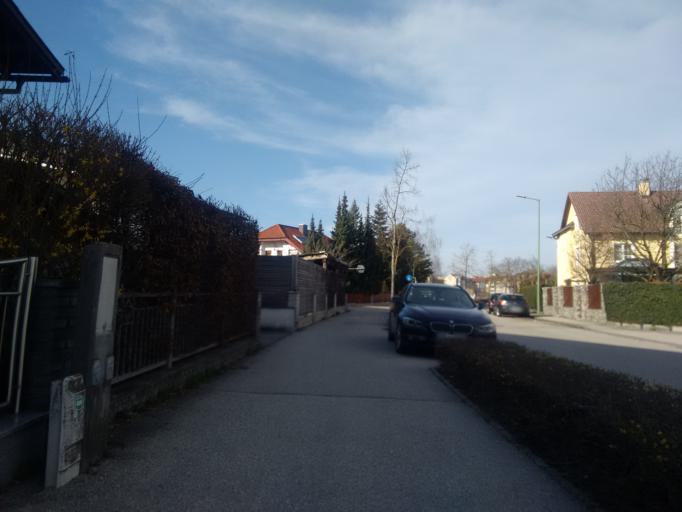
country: AT
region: Upper Austria
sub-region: Wels Stadt
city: Wels
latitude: 48.1751
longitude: 14.0136
